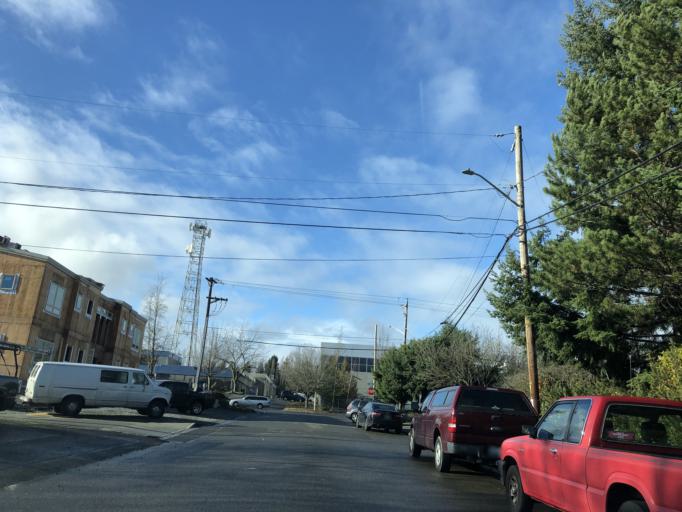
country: US
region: Washington
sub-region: Pierce County
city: Tacoma
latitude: 47.2392
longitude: -122.4643
